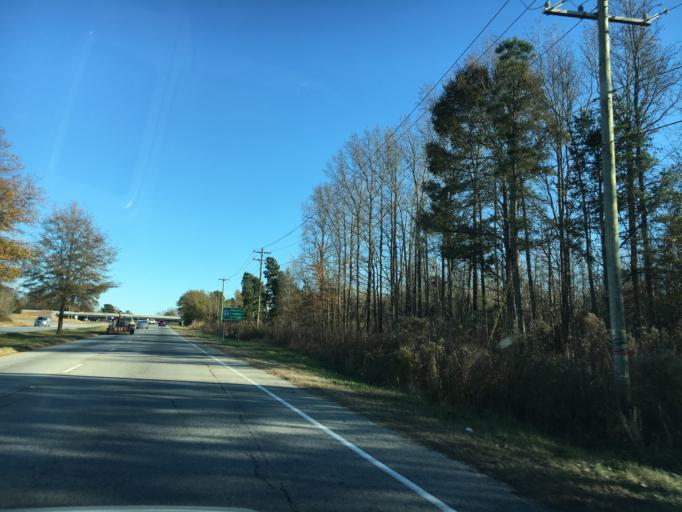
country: US
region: South Carolina
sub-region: Spartanburg County
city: Wellford
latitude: 34.9404
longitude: -82.0797
